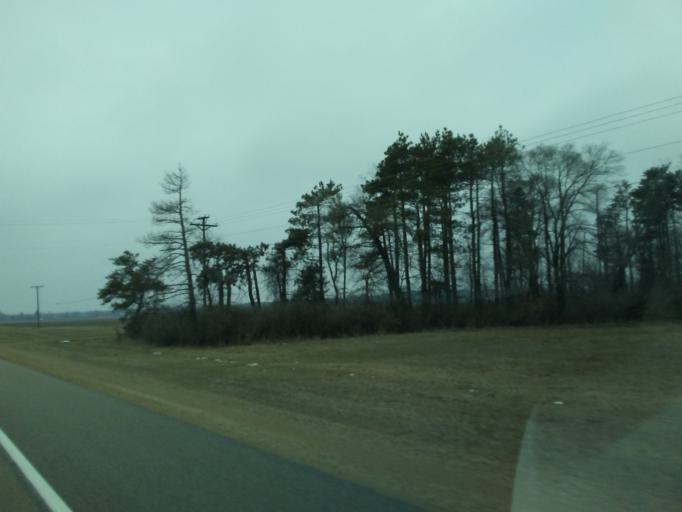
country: US
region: Wisconsin
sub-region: Sauk County
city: Spring Green
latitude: 43.1617
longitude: -90.0048
